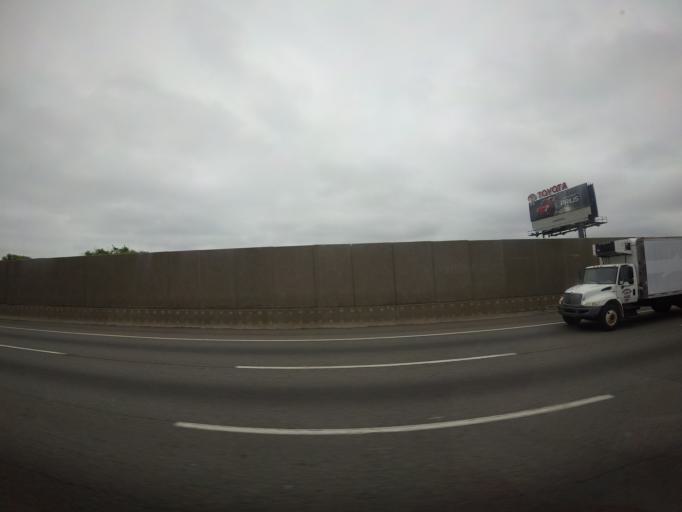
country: US
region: New Jersey
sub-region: Union County
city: Elizabeth
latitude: 40.6546
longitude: -74.1907
